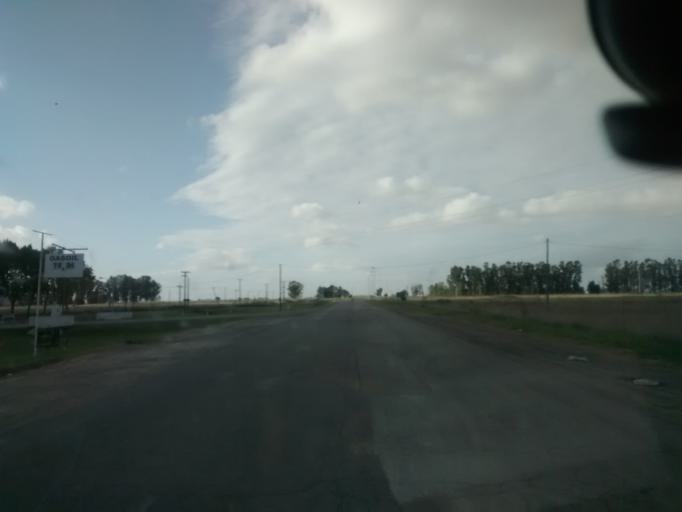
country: AR
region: Buenos Aires
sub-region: Partido de Ayacucho
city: Ayacucho
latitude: -37.1316
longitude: -58.5521
